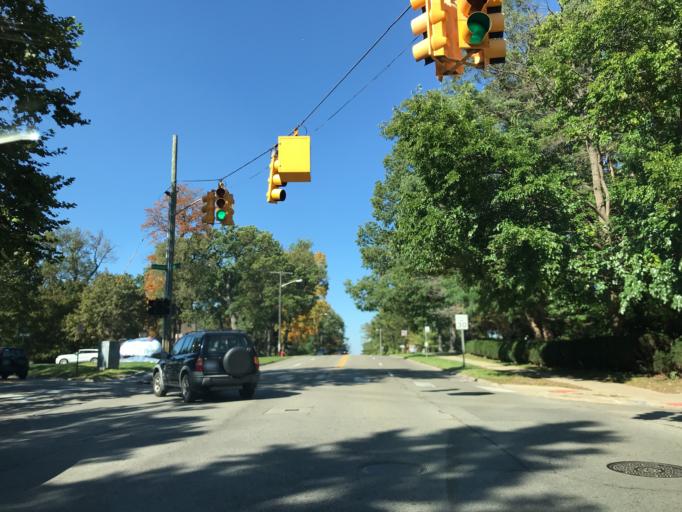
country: US
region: Michigan
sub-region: Washtenaw County
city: Ann Arbor
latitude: 42.2723
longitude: -83.7279
